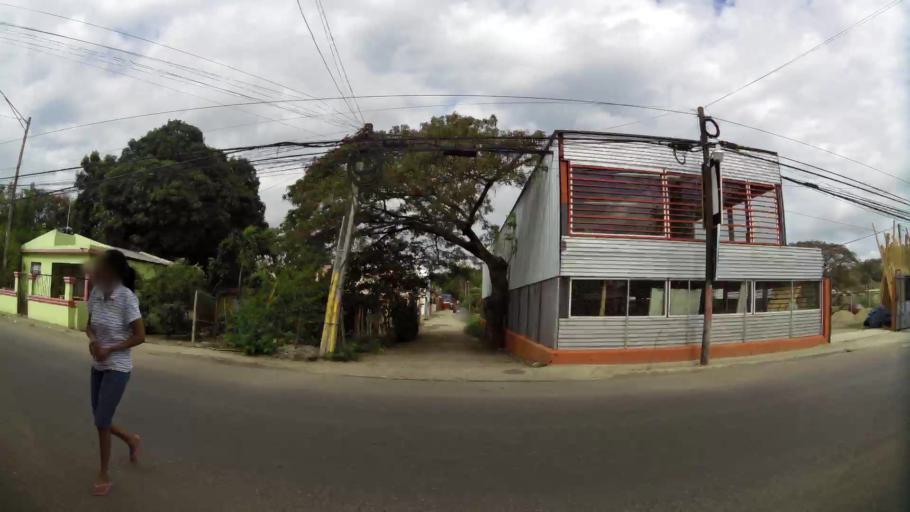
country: DO
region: Santiago
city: Santiago de los Caballeros
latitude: 19.4158
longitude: -70.7173
